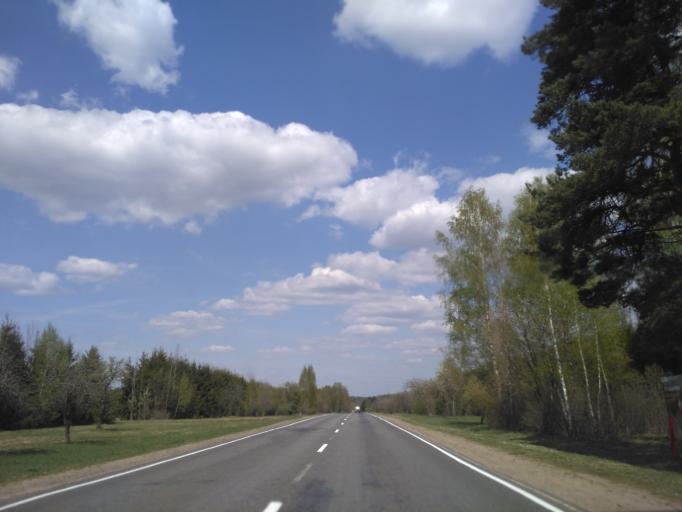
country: BY
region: Minsk
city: Vilyeyka
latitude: 54.6827
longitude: 26.9213
